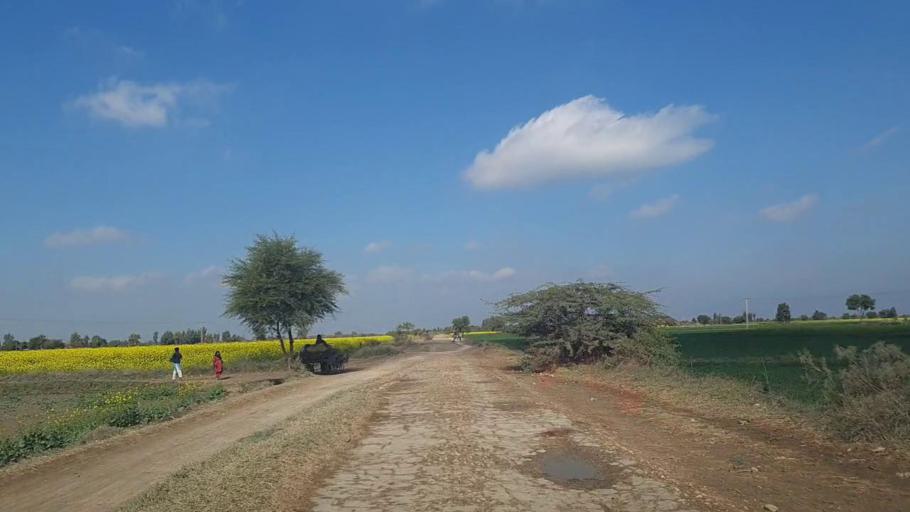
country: PK
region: Sindh
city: Sanghar
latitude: 26.0704
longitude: 68.9865
